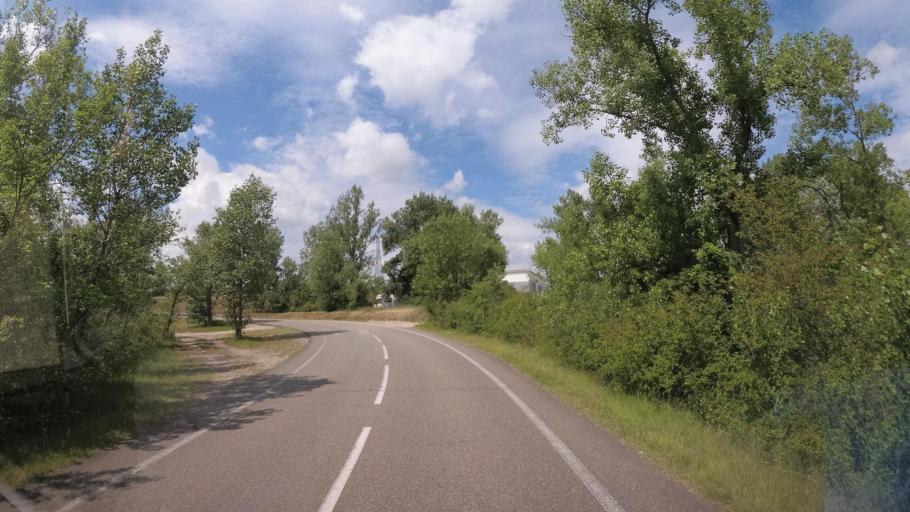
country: FR
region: Alsace
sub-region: Departement du Haut-Rhin
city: Fessenheim
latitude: 47.9142
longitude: 7.5753
